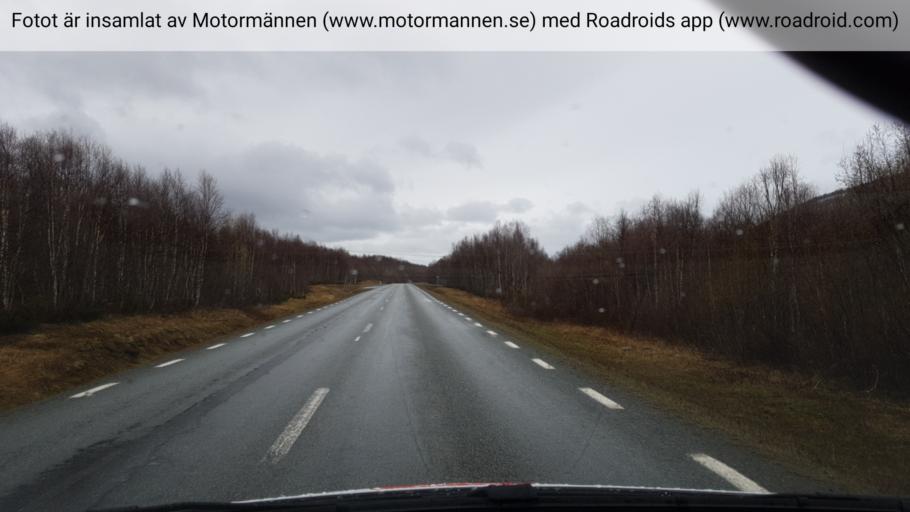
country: NO
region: Nordland
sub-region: Rana
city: Mo i Rana
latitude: 65.7949
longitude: 15.1000
